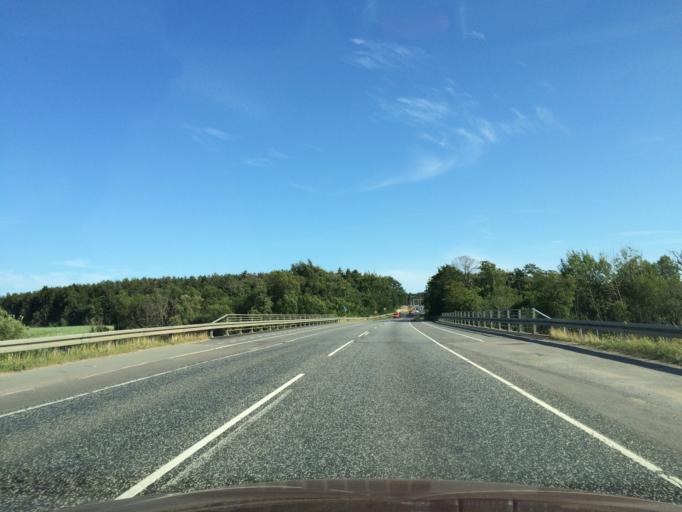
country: DK
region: Central Jutland
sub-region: Silkeborg Kommune
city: Svejbaek
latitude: 56.1745
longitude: 9.5994
